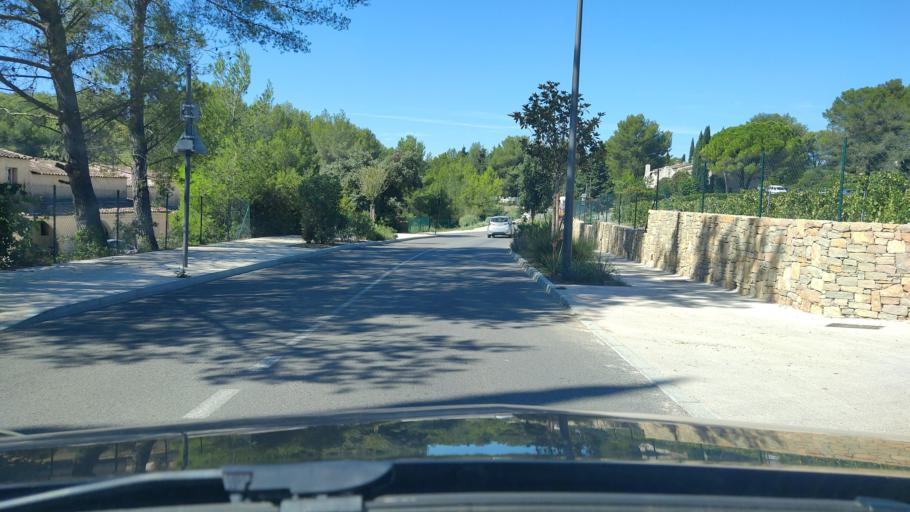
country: FR
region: Provence-Alpes-Cote d'Azur
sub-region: Departement du Var
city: Sanary-sur-Mer
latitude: 43.1420
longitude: 5.7788
